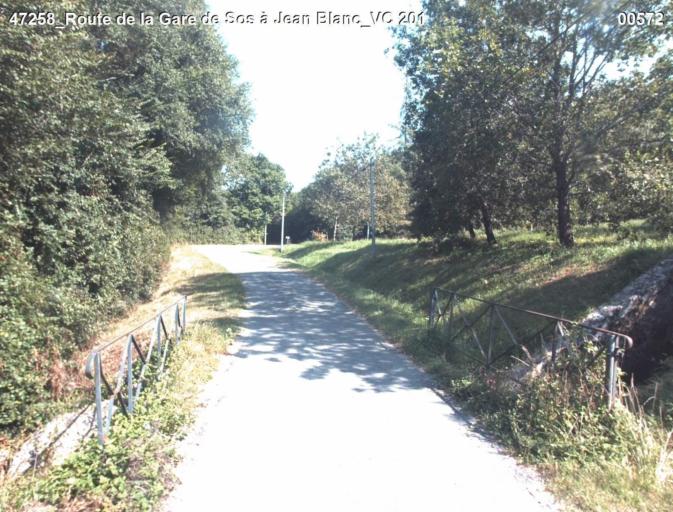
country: FR
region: Midi-Pyrenees
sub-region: Departement du Gers
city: Montreal
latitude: 44.0375
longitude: 0.1498
